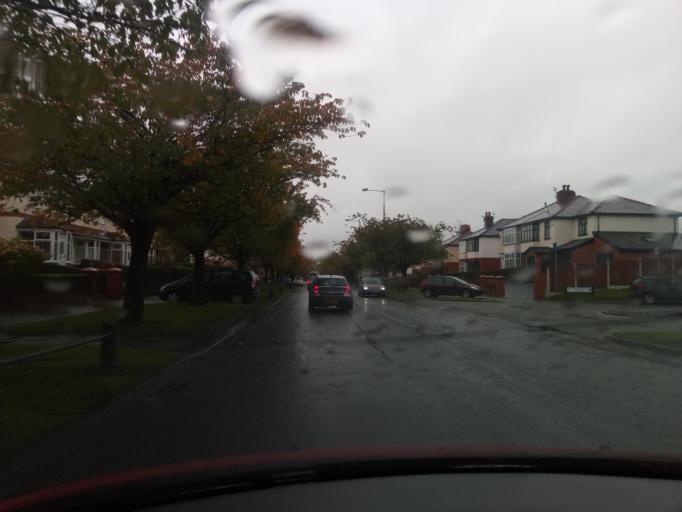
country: GB
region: England
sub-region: Lancashire
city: Preston
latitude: 53.7729
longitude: -2.6815
